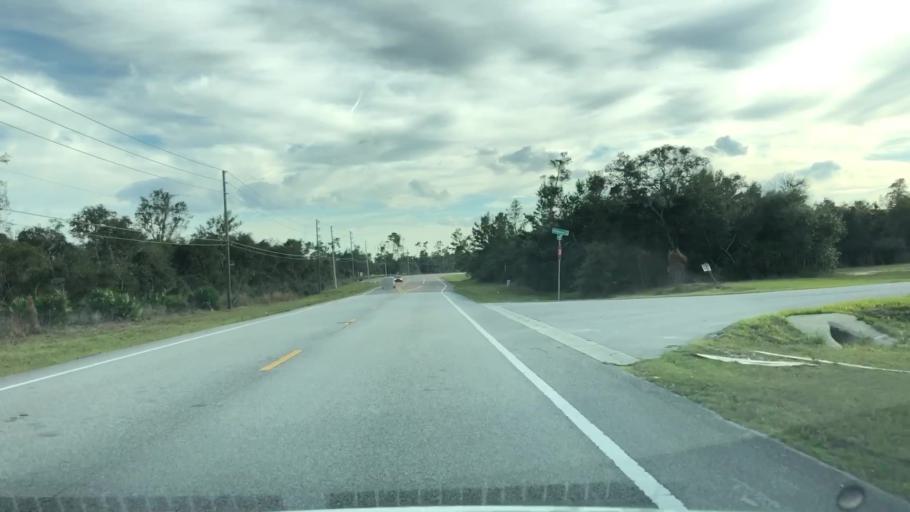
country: US
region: Florida
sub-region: Volusia County
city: Lake Helen
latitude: 28.9452
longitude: -81.2554
